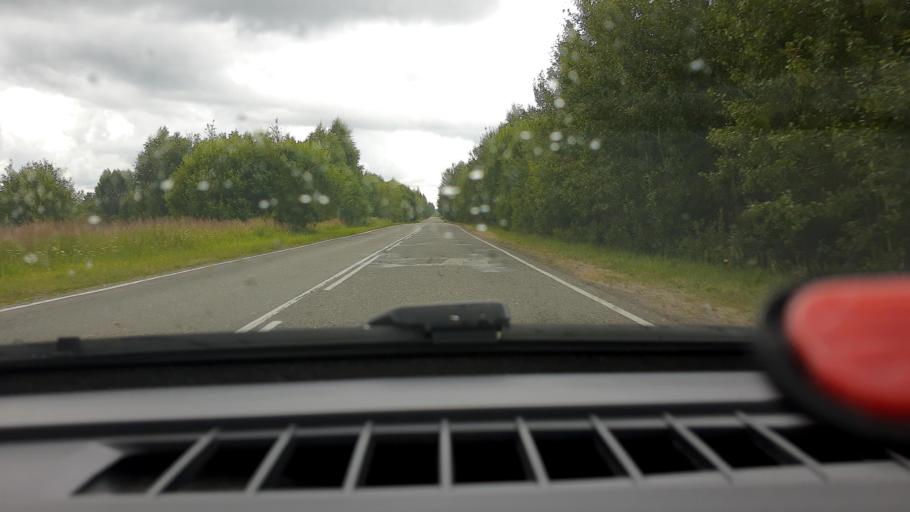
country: RU
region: Nizjnij Novgorod
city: Neklyudovo
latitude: 56.5070
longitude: 43.9701
